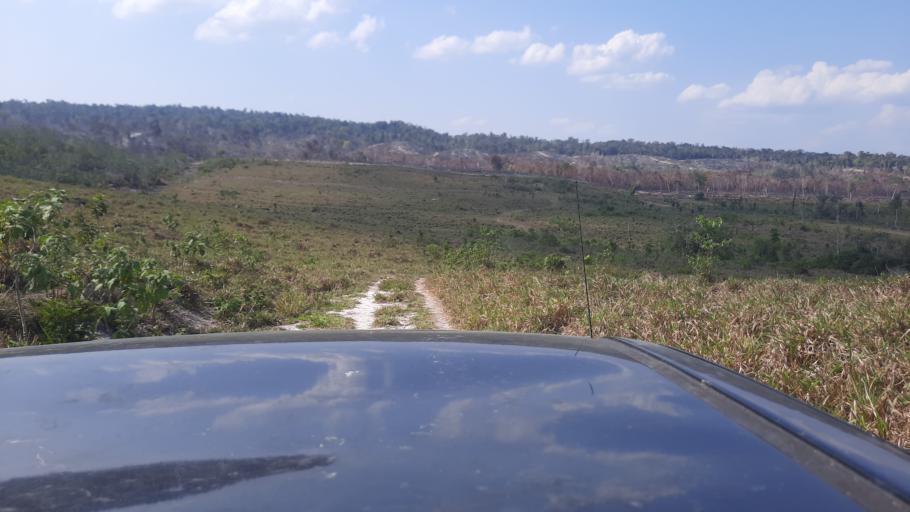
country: BZ
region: Cayo
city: Valley of Peace
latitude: 17.4002
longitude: -89.0402
